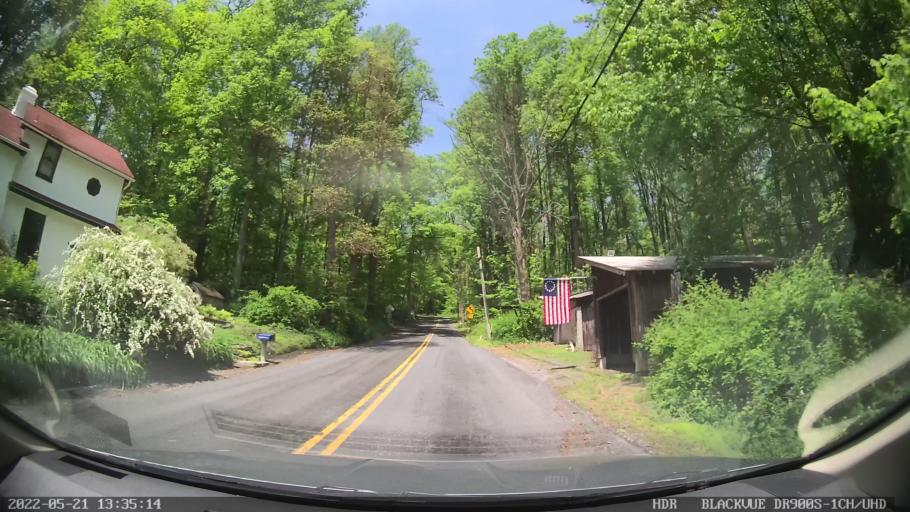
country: US
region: Pennsylvania
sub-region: Berks County
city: Topton
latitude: 40.4475
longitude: -75.6774
